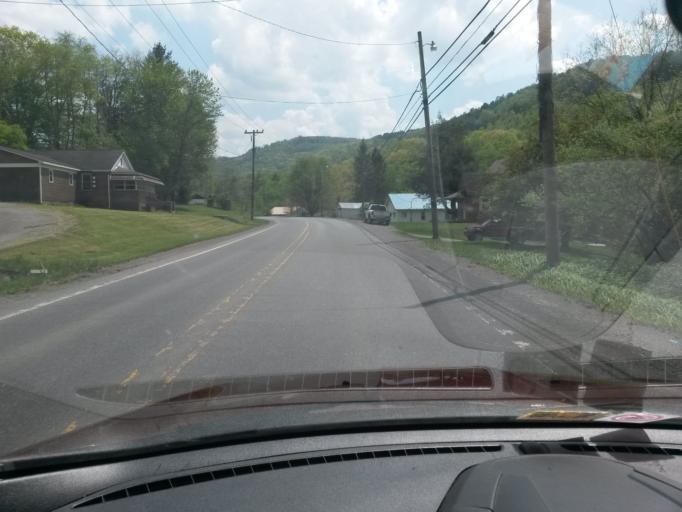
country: US
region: West Virginia
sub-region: Greenbrier County
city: Rainelle
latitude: 37.9977
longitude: -80.7368
